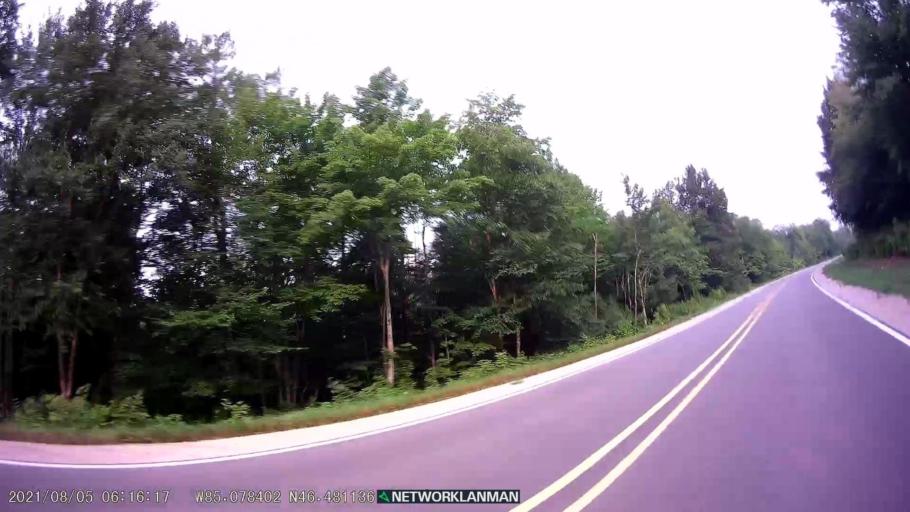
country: US
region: Michigan
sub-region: Luce County
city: Newberry
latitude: 46.4823
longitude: -85.0800
